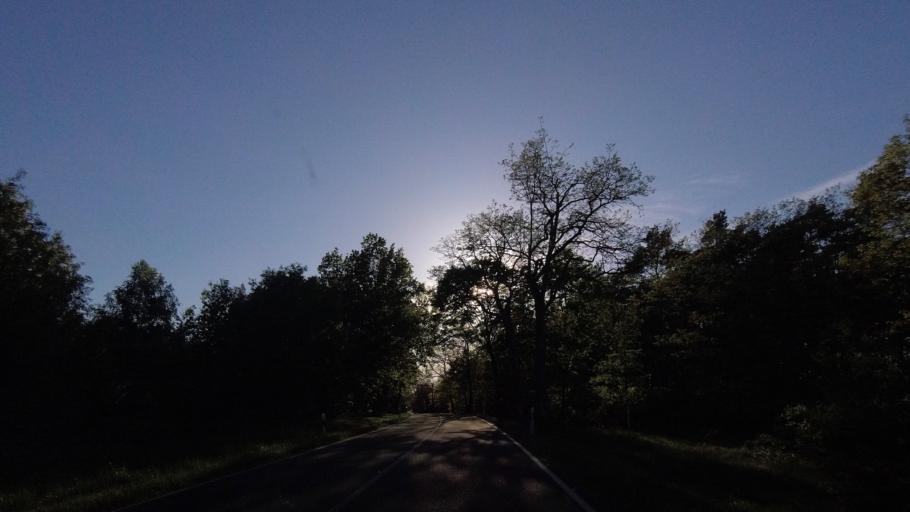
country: DE
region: Brandenburg
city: Ihlow
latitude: 51.9861
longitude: 13.3364
